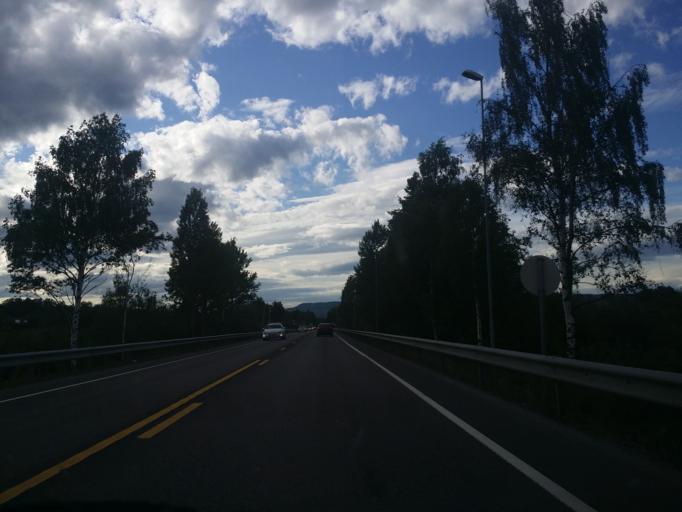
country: NO
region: Hedmark
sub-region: Hamar
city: Hamar
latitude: 60.8041
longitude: 11.1126
